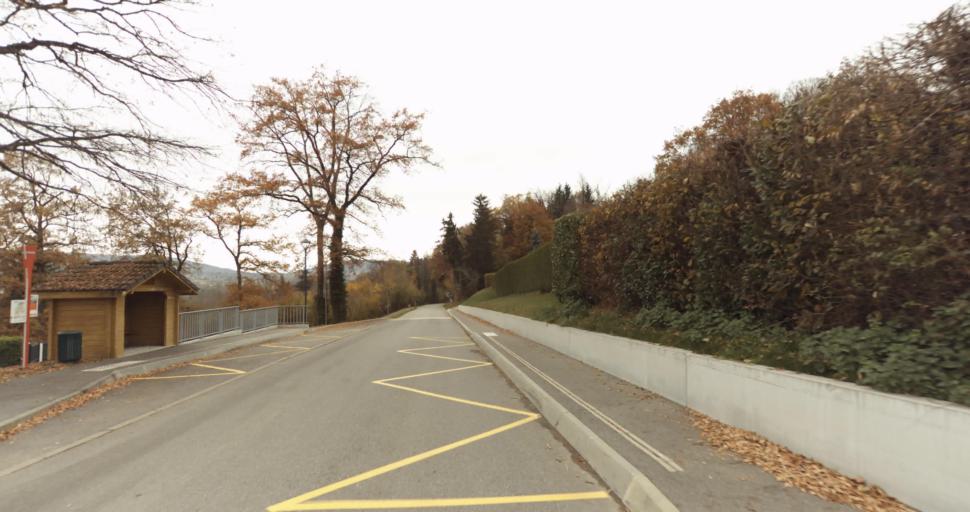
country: FR
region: Rhone-Alpes
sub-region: Departement de la Haute-Savoie
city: Saint-Martin-Bellevue
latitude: 45.9660
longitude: 6.1398
